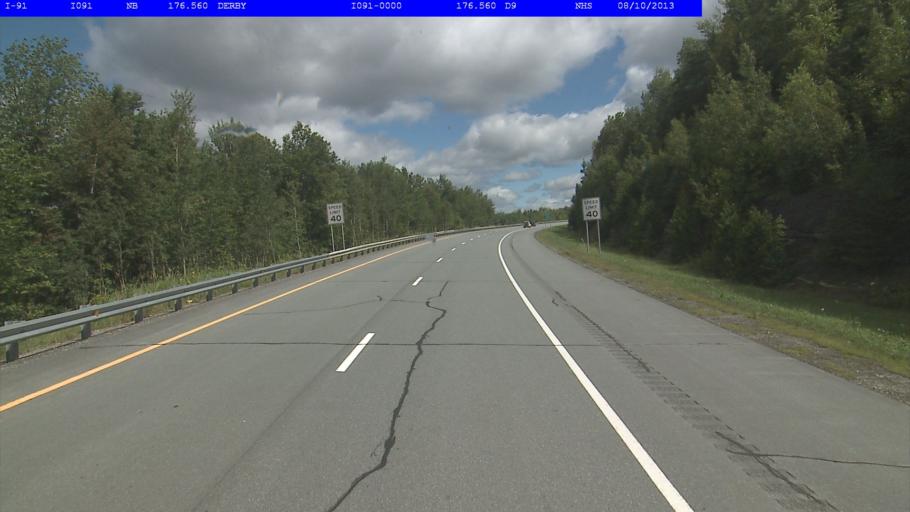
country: US
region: Vermont
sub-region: Orleans County
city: Newport
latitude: 44.9977
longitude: -72.1010
